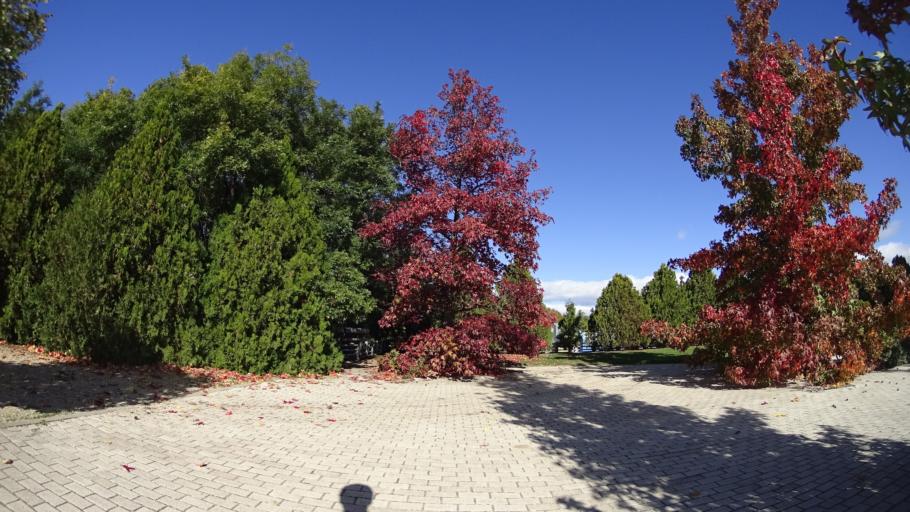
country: ES
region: Madrid
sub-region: Provincia de Madrid
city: San Blas
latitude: 40.4642
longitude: -3.6097
